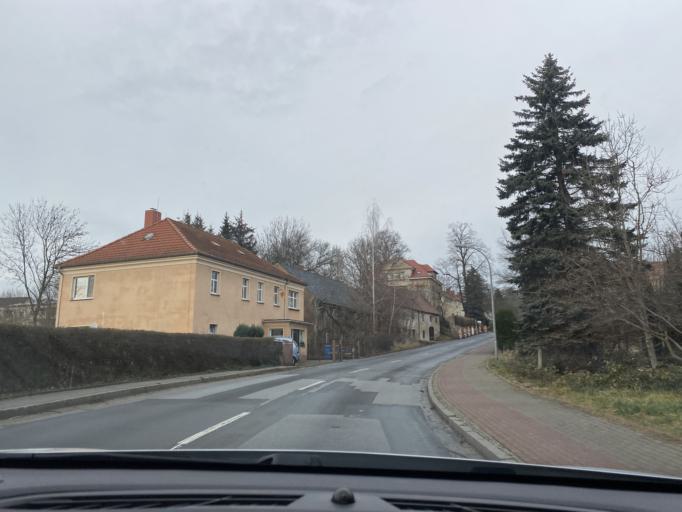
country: DE
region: Saxony
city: Reichenbach
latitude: 51.1413
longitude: 14.7974
